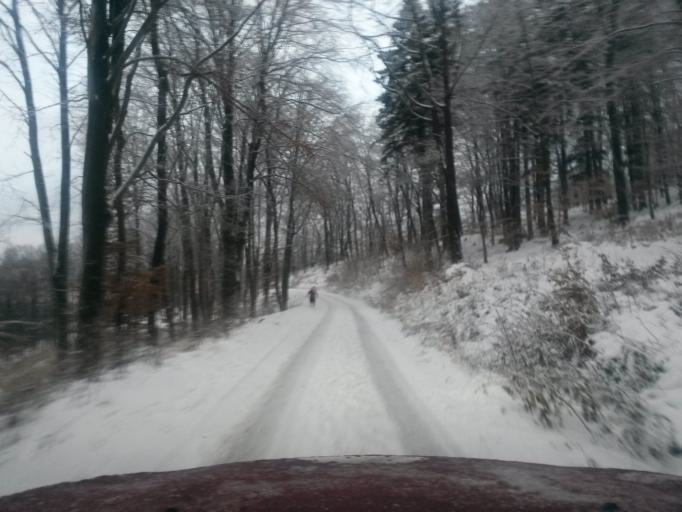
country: SK
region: Kosicky
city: Kosice
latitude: 48.7607
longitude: 21.1214
